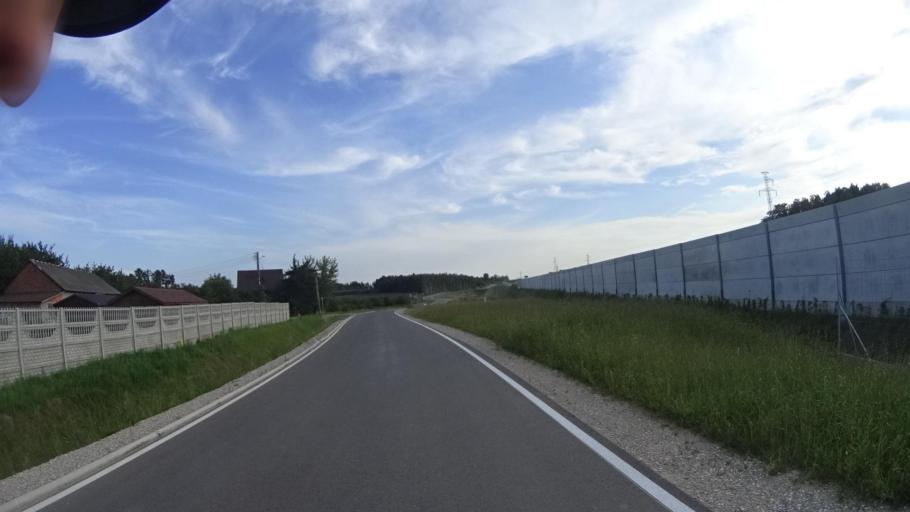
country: PL
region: Masovian Voivodeship
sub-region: Powiat piaseczynski
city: Tarczyn
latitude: 51.9634
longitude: 20.8573
